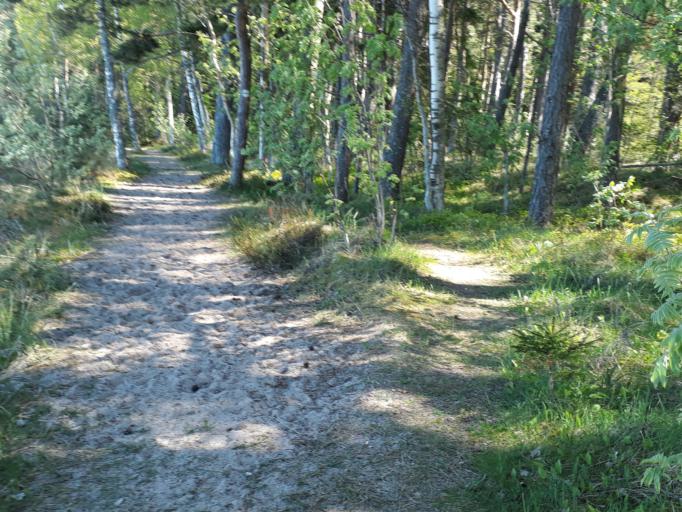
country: EE
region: Laeaene-Virumaa
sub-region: Haljala vald
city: Haljala
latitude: 59.5856
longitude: 26.1186
